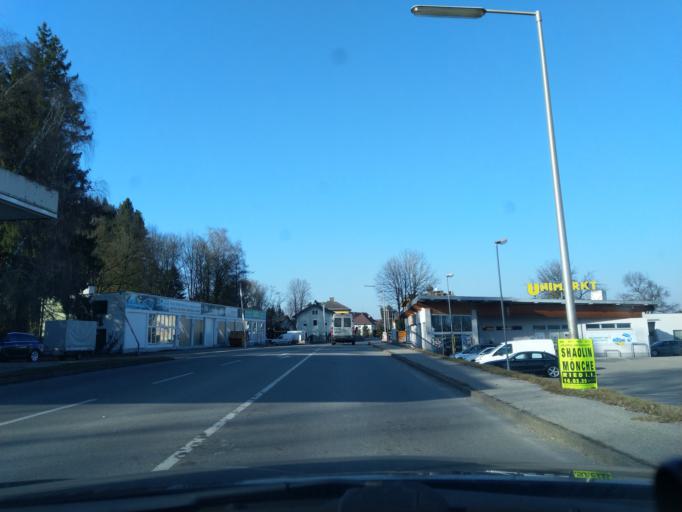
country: AT
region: Upper Austria
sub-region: Politischer Bezirk Ried im Innkreis
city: Ried im Innkreis
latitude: 48.2444
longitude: 13.4581
